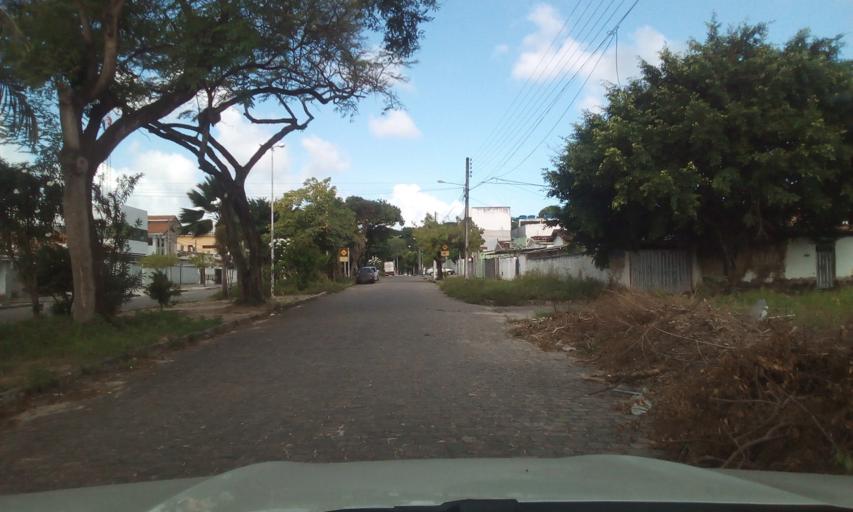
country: BR
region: Paraiba
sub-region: Joao Pessoa
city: Joao Pessoa
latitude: -7.1327
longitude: -34.8505
